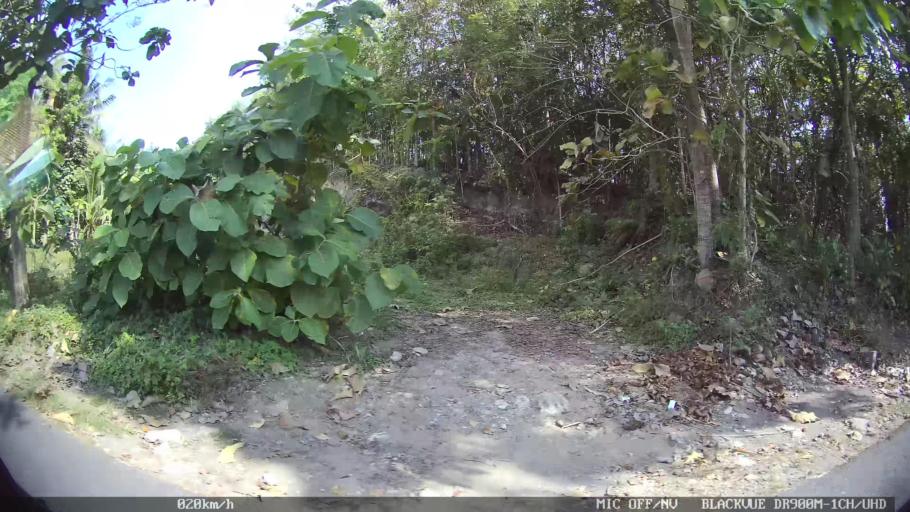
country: ID
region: Daerah Istimewa Yogyakarta
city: Kasihan
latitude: -7.8492
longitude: 110.2991
